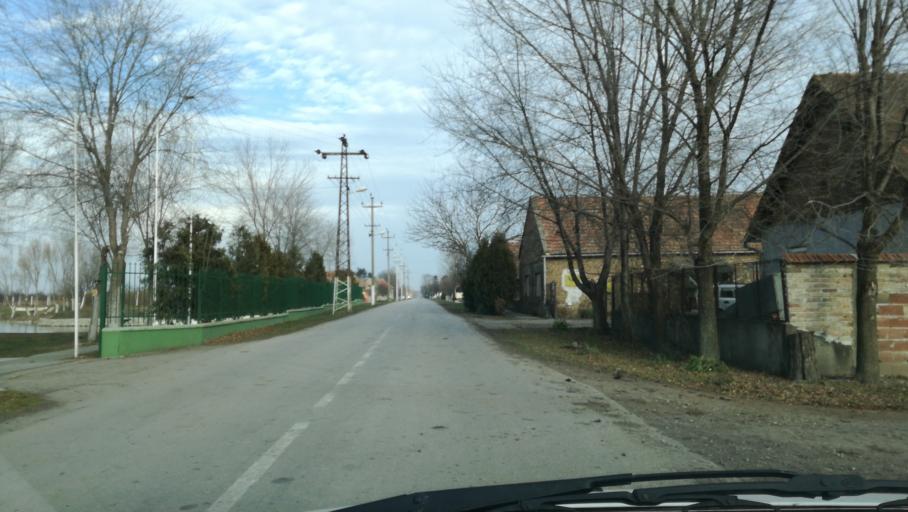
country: RS
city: Rusko Selo
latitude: 45.7482
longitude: 20.5599
